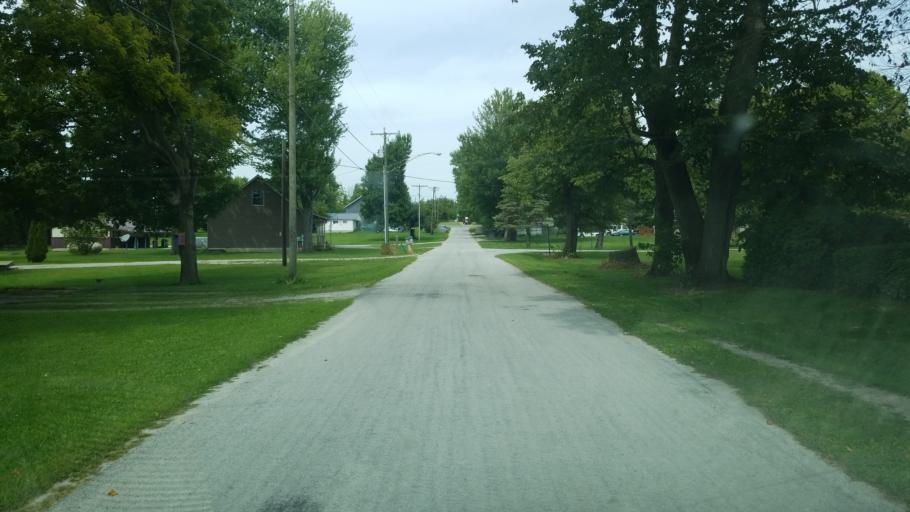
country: US
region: Ohio
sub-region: Hardin County
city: Kenton
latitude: 40.6195
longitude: -83.4683
